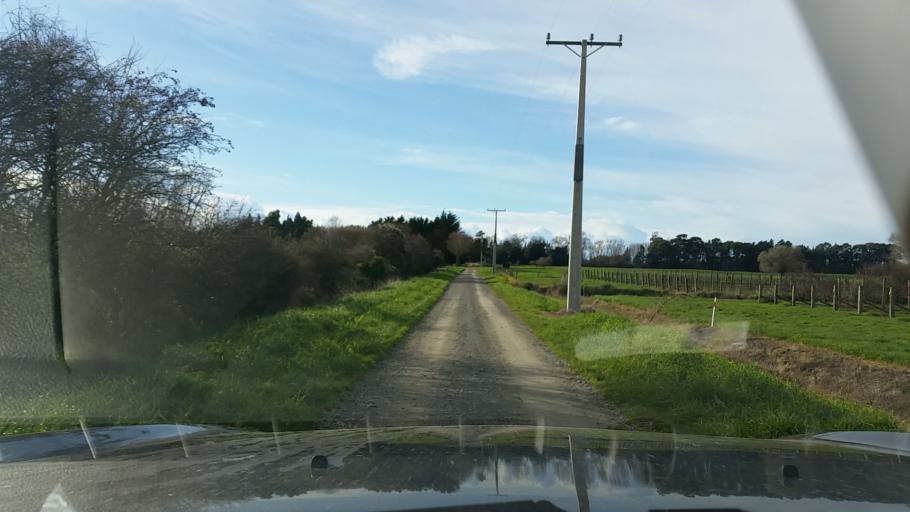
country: NZ
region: Marlborough
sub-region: Marlborough District
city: Blenheim
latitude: -41.4308
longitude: 173.9906
